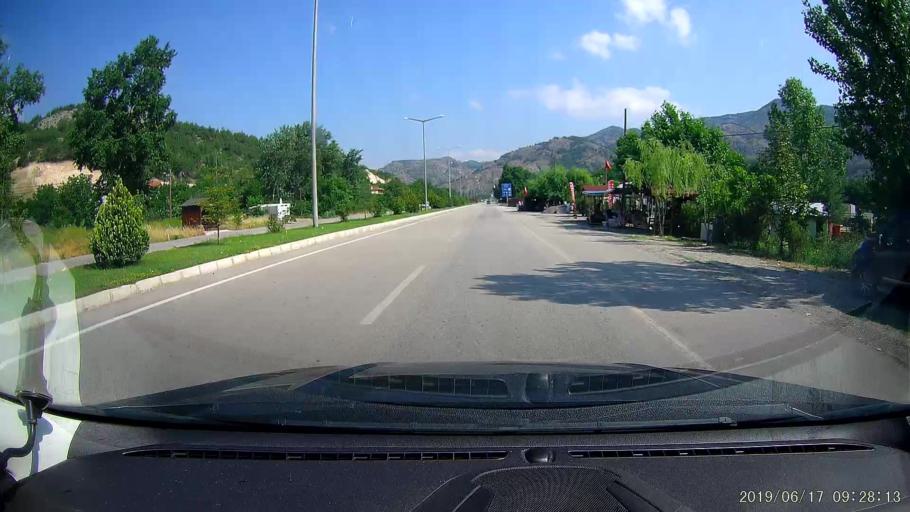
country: TR
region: Amasya
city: Amasya
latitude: 40.6856
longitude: 35.8229
